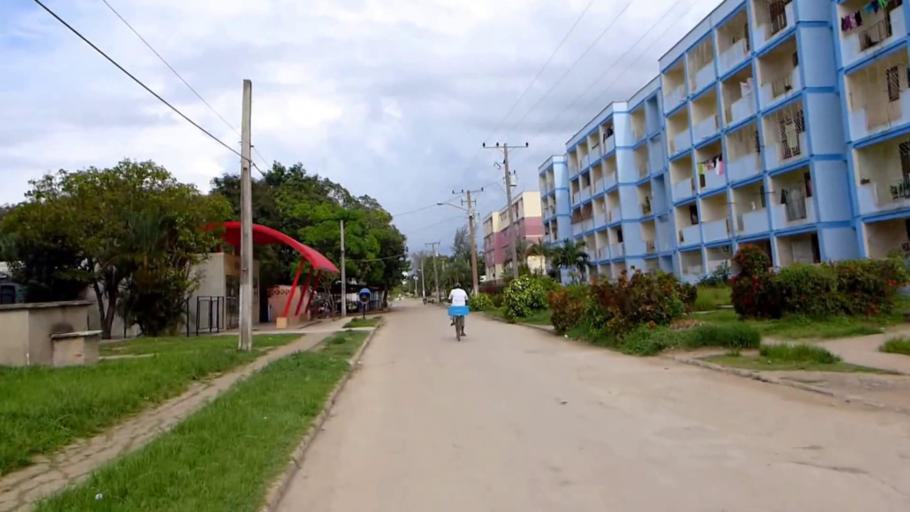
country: CU
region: Camaguey
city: Camaguey
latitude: 21.3637
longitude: -77.8944
